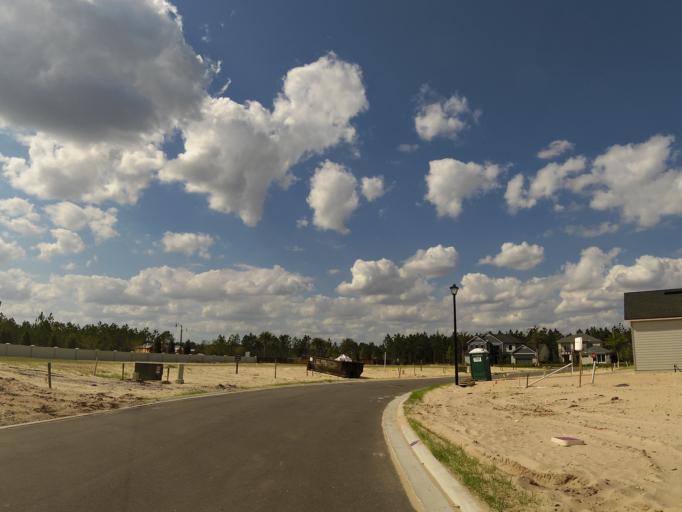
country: US
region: Florida
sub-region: Saint Johns County
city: Palm Valley
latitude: 30.1957
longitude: -81.5065
